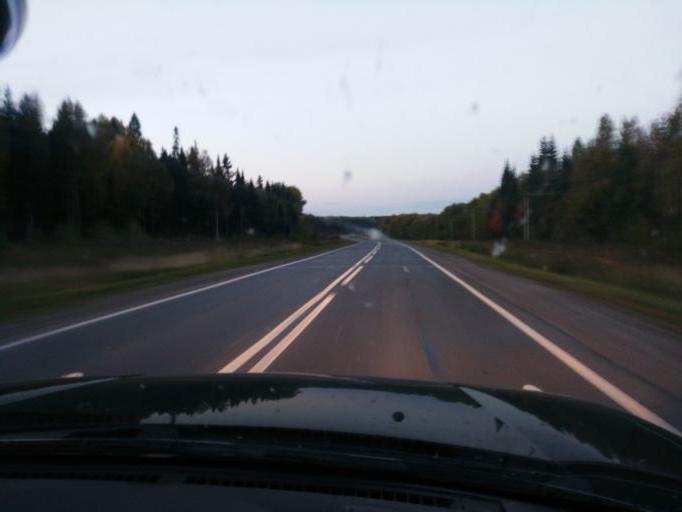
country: RU
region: Perm
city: Verkhnechusovskiye Gorodki
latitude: 58.2328
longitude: 57.2134
